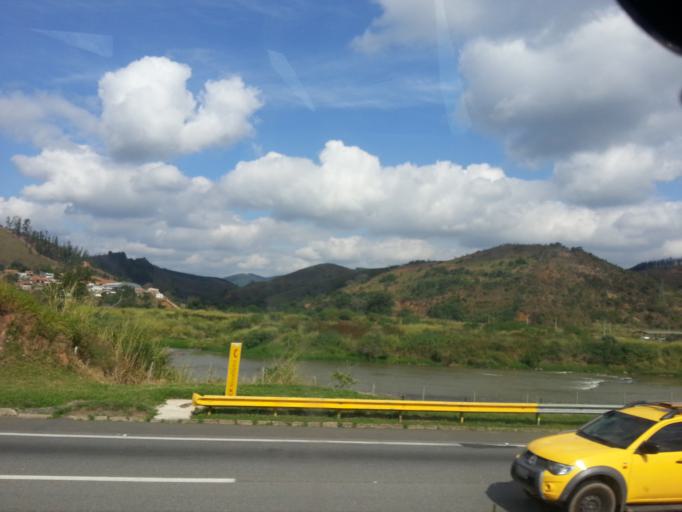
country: BR
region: Sao Paulo
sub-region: Cruzeiro
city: Cruzeiro
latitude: -22.5438
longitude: -44.7895
